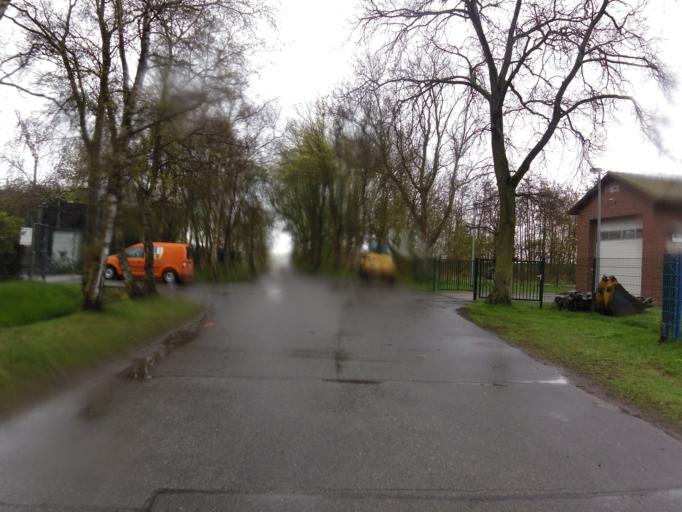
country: DE
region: Mecklenburg-Vorpommern
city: Zingst
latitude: 54.4317
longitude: 12.7051
